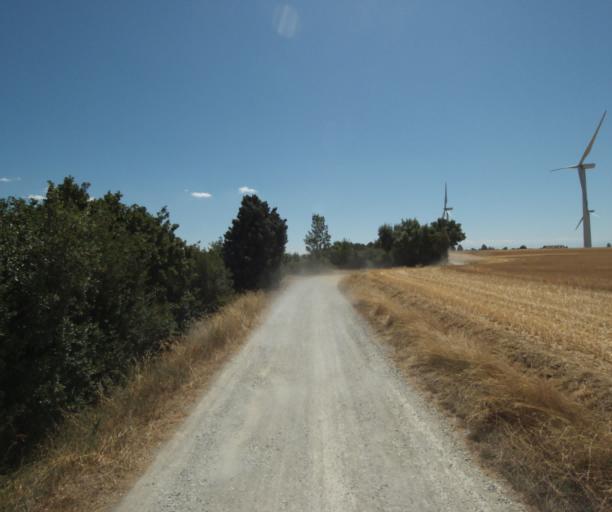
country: FR
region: Midi-Pyrenees
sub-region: Departement de la Haute-Garonne
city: Saint-Felix-Lauragais
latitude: 43.4668
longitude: 1.9210
